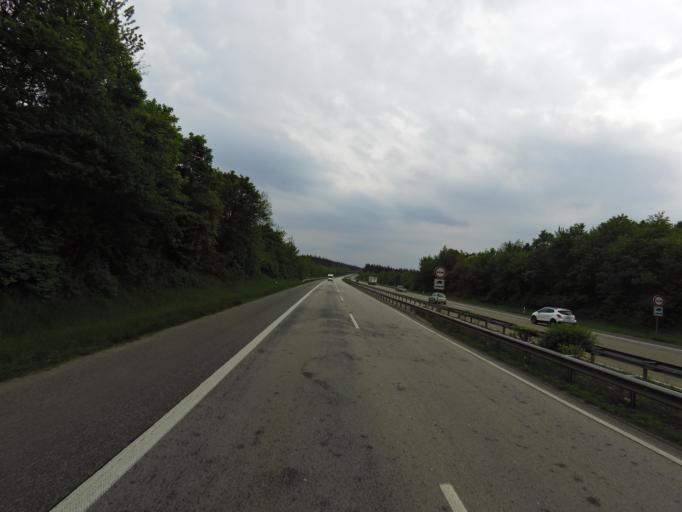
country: DE
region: Rheinland-Pfalz
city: Dorth
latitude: 50.1808
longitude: 7.5930
